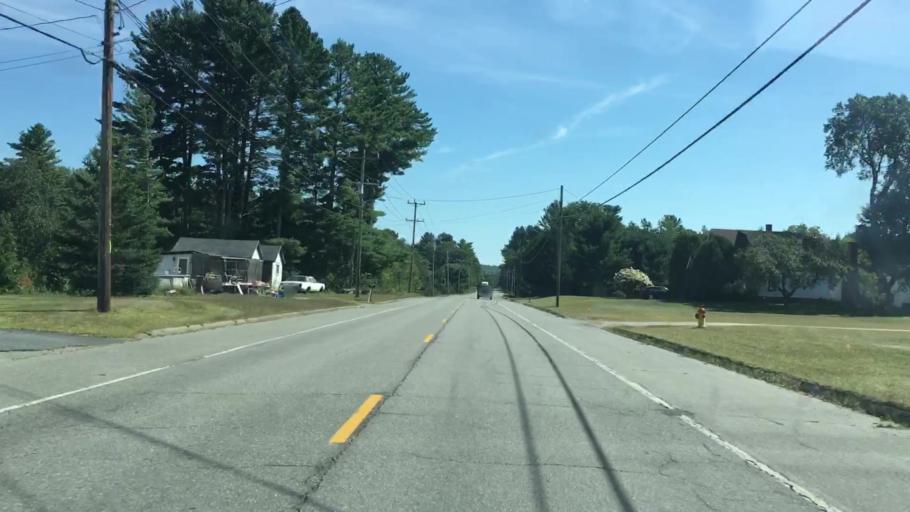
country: US
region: Maine
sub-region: Piscataquis County
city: Milo
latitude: 45.2389
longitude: -68.9666
